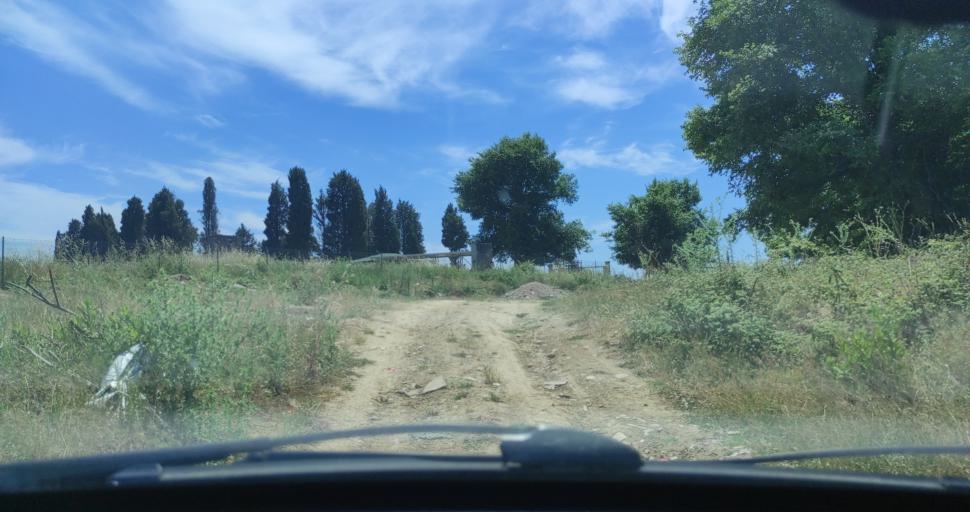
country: AL
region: Shkoder
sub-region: Rrethi i Shkodres
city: Velipoje
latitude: 41.8836
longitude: 19.3847
